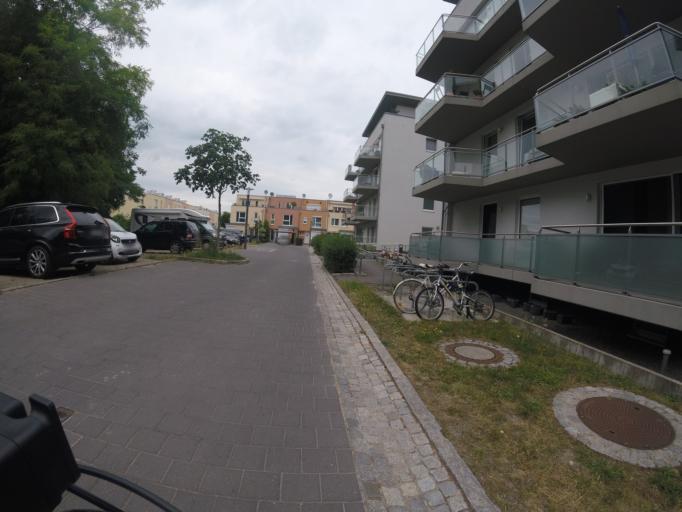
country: DE
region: Berlin
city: Hakenfelde
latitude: 52.5531
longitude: 13.2150
